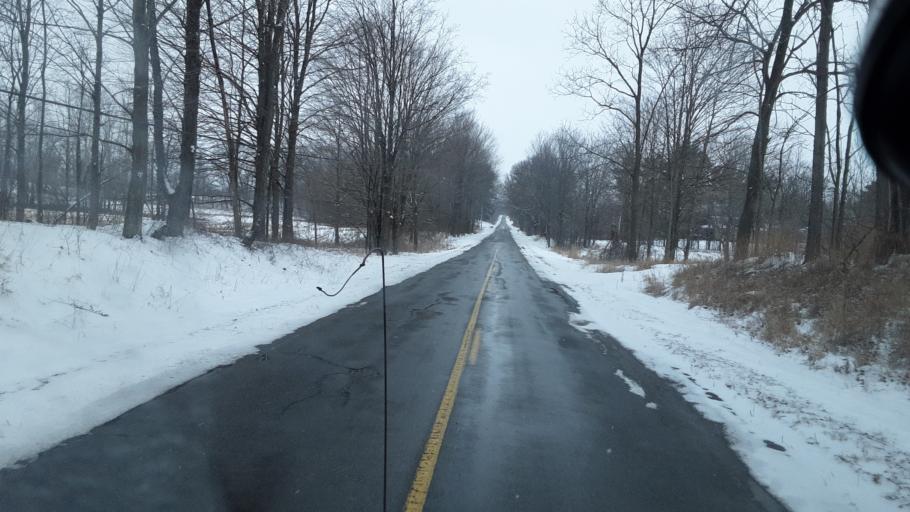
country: US
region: Michigan
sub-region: Ingham County
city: Leslie
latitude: 42.4367
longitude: -84.4499
